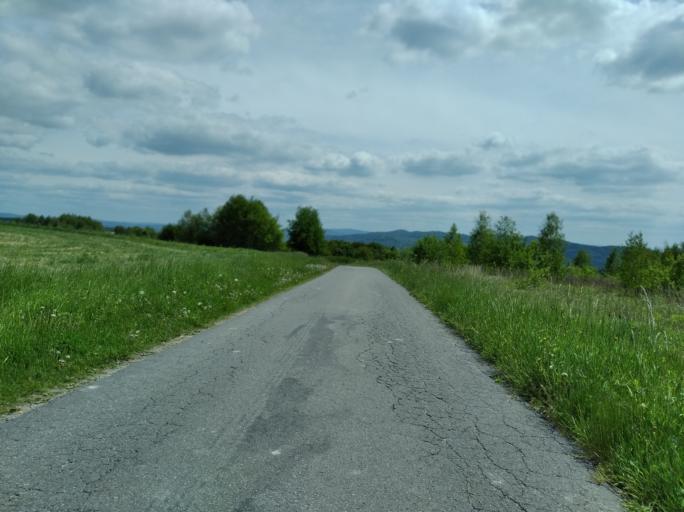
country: PL
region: Subcarpathian Voivodeship
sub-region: Powiat strzyzowski
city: Wisniowa
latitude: 49.8911
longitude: 21.6217
